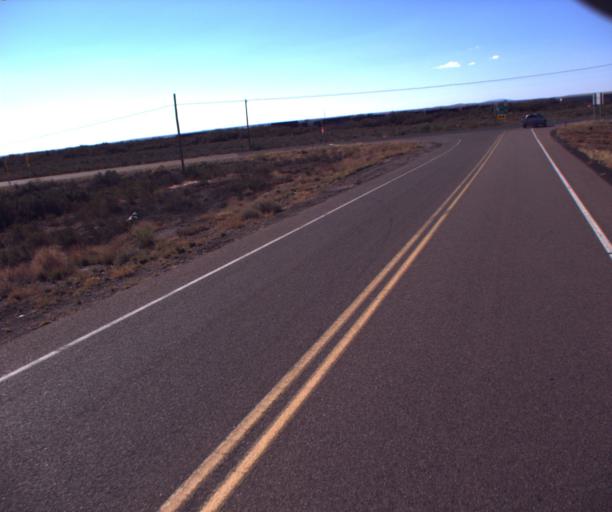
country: US
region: Arizona
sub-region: Navajo County
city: Winslow
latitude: 35.0065
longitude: -110.6432
